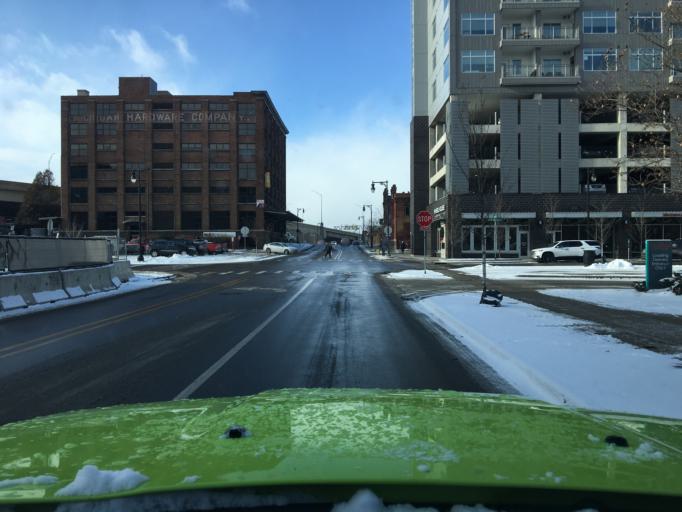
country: US
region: Michigan
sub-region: Kent County
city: Grand Rapids
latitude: 42.9610
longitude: -85.6719
